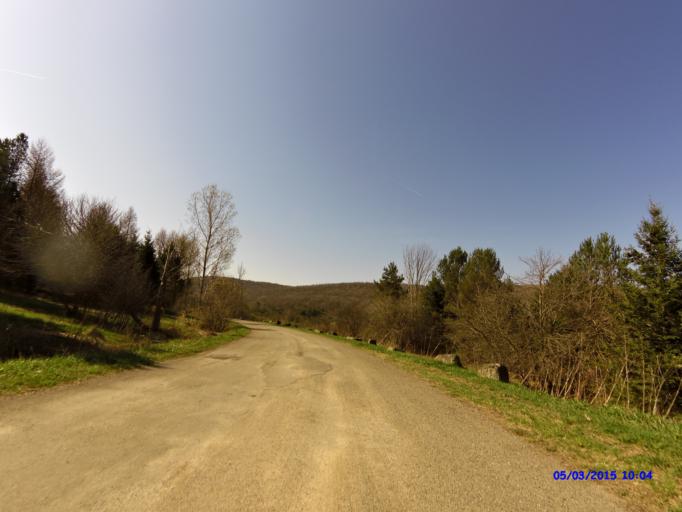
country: US
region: New York
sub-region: Cattaraugus County
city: Franklinville
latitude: 42.3224
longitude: -78.4344
